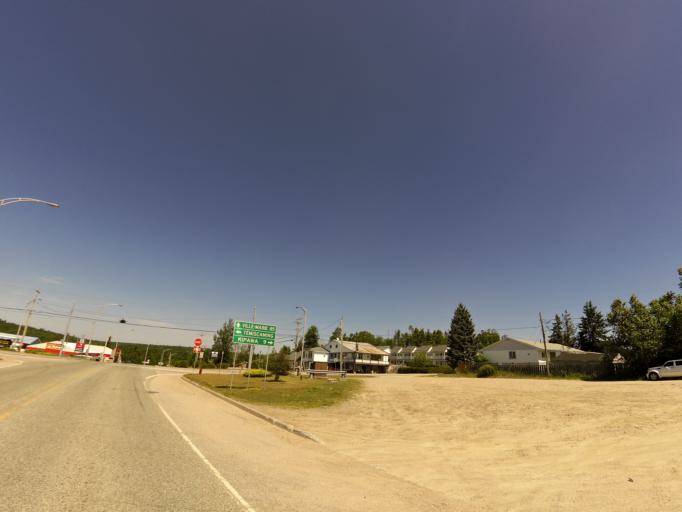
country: CA
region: Quebec
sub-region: Abitibi-Temiscamingue
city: Temiscaming
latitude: 46.7371
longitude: -79.0659
